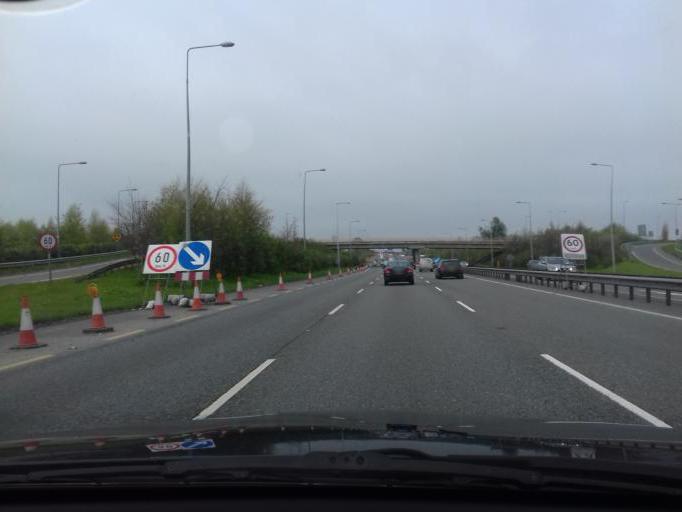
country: IE
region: Leinster
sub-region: Kildare
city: Johnstown
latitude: 53.2424
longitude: -6.6100
